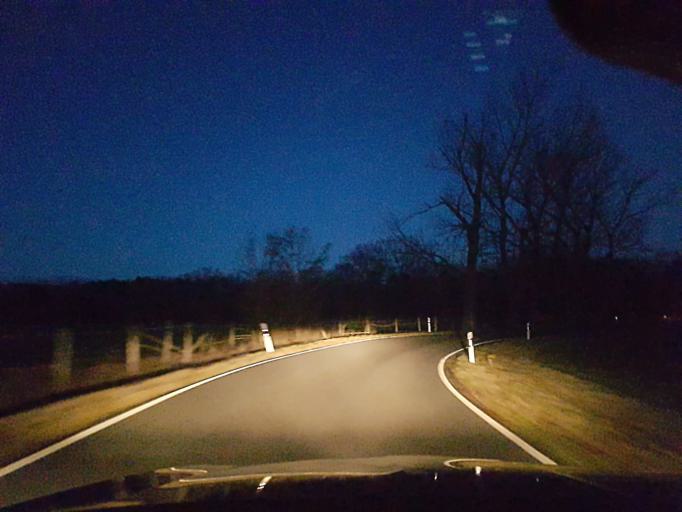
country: DE
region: Brandenburg
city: Schilda
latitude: 51.5688
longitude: 13.3461
